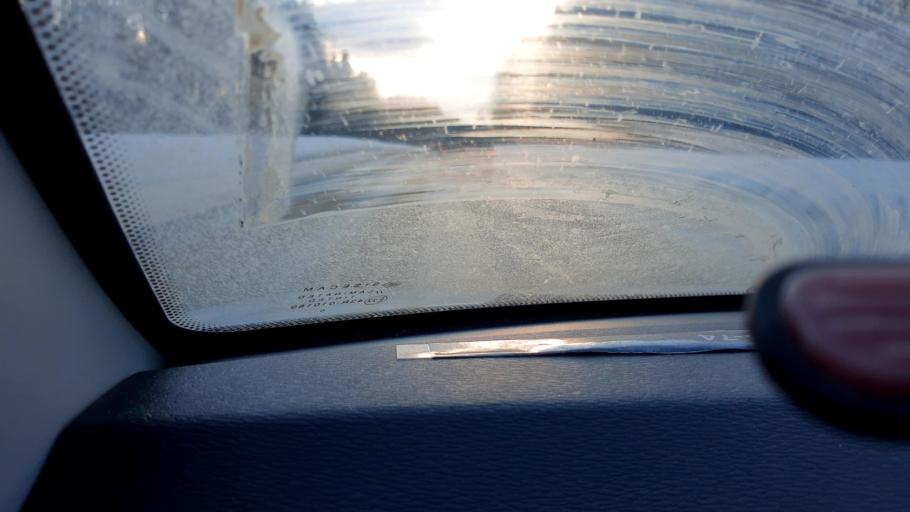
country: RU
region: Nizjnij Novgorod
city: Krasnyye Baki
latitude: 57.1804
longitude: 45.3710
